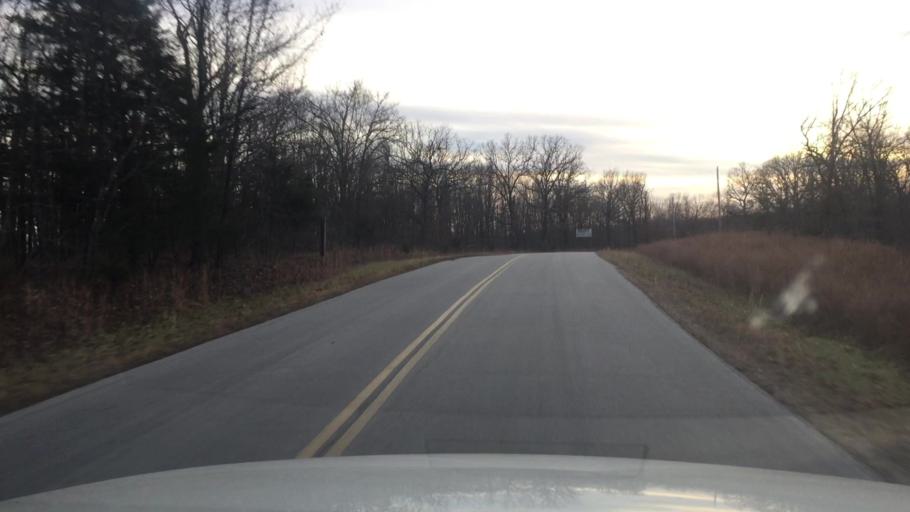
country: US
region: Missouri
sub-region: Morgan County
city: Versailles
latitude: 38.3336
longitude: -92.7686
